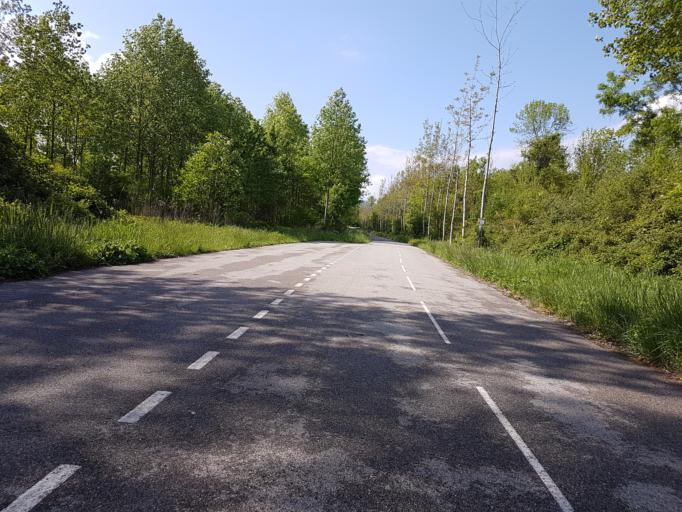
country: FR
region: Rhone-Alpes
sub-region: Departement de l'Ain
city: Culoz
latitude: 45.8546
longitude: 5.8207
